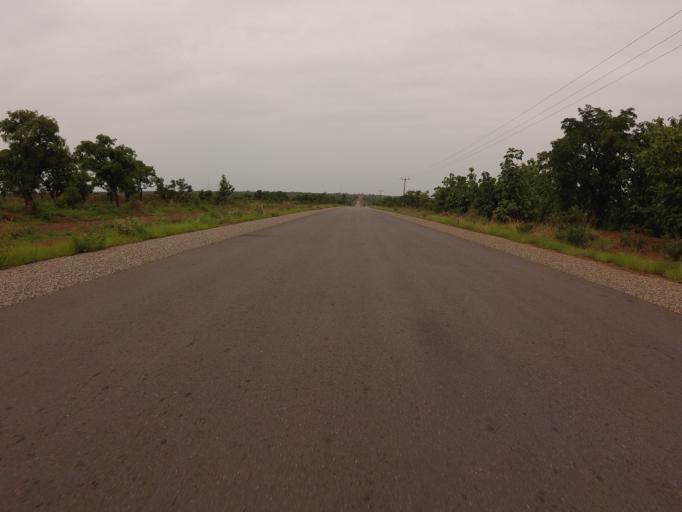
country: GH
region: Northern
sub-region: Yendi
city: Yendi
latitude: 9.2353
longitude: 0.0203
